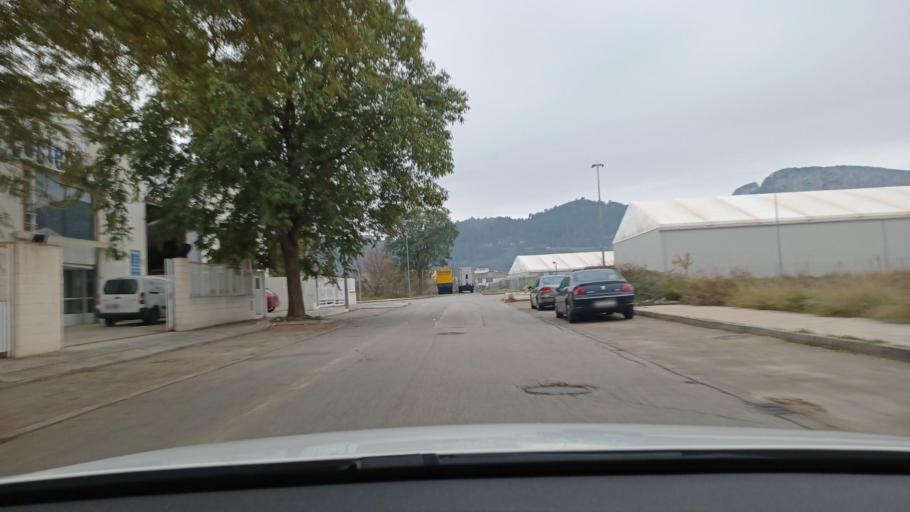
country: ES
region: Valencia
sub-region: Provincia de Valencia
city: Xativa
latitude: 38.9973
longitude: -0.5077
